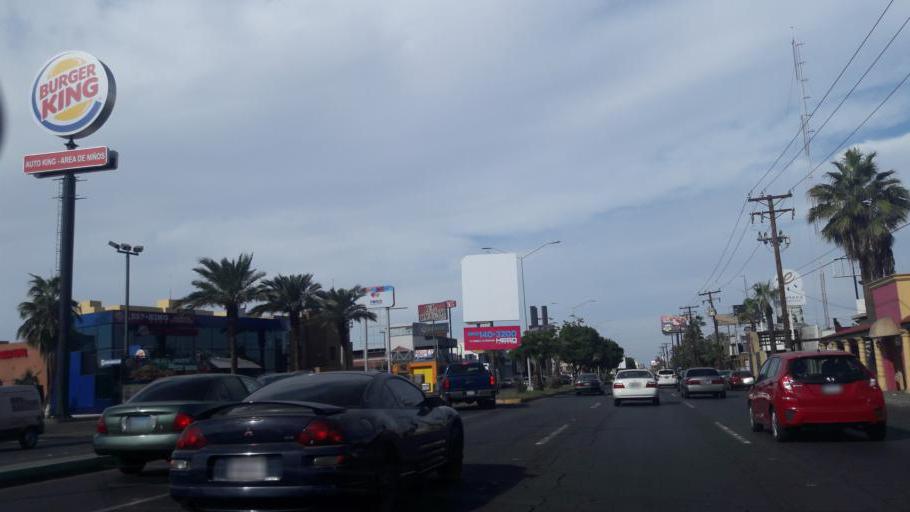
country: MX
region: Baja California
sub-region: Mexicali
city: Mexicali
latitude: 32.6397
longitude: -115.4493
